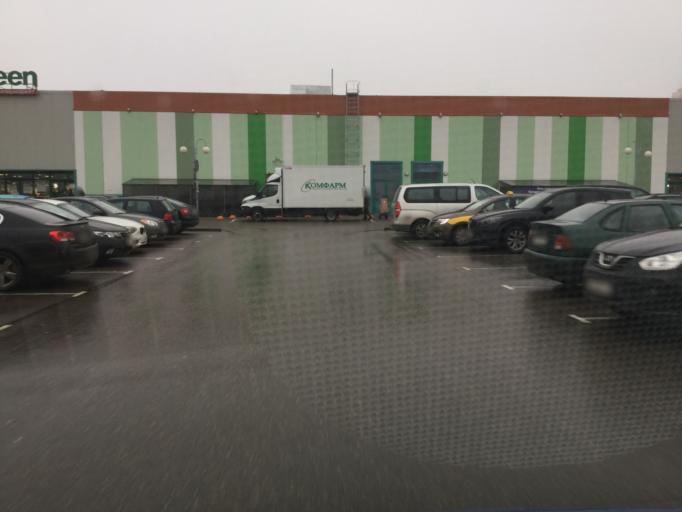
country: BY
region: Vitebsk
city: Vitebsk
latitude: 55.1628
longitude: 30.2069
